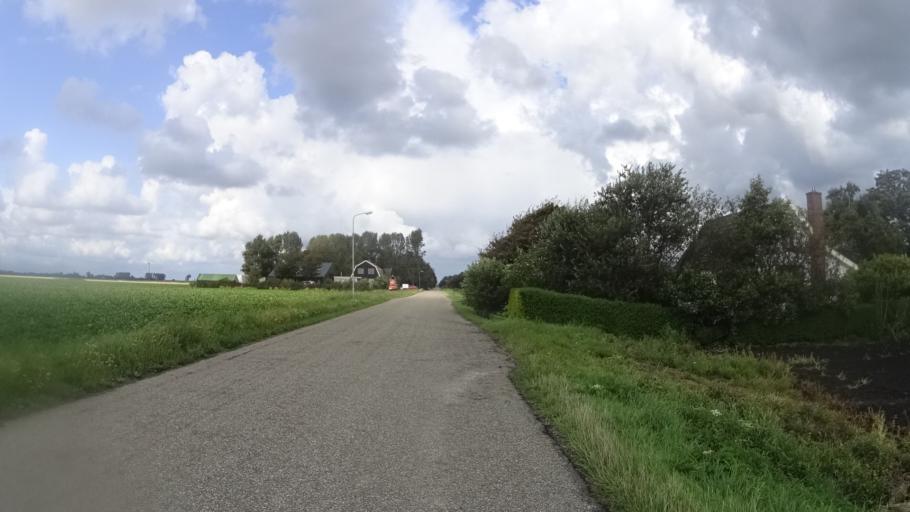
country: NL
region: North Holland
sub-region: Gemeente Schagen
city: Schagen
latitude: 52.8493
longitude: 4.8802
